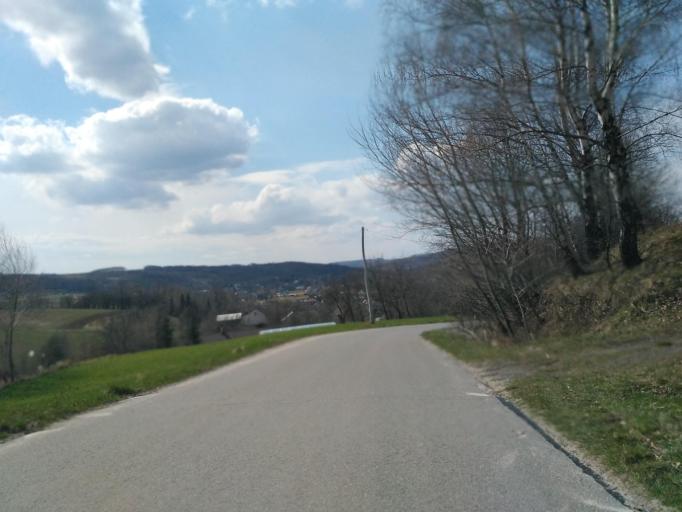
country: PL
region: Subcarpathian Voivodeship
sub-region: Powiat ropczycko-sedziszowski
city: Sedziszow Malopolski
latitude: 50.0427
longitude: 21.7075
